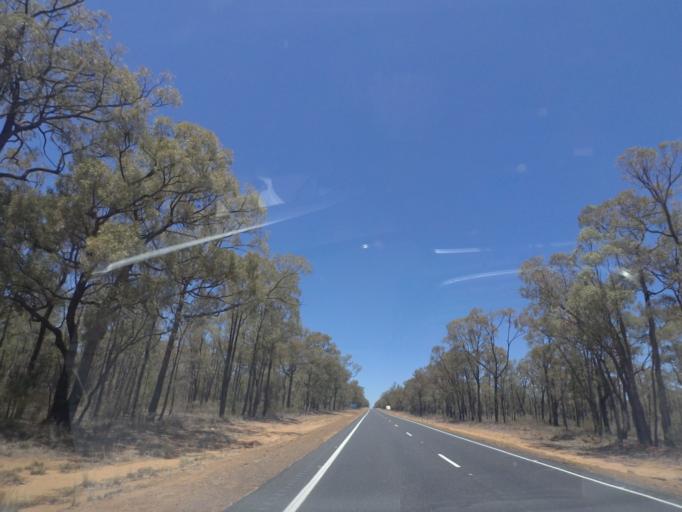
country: AU
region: New South Wales
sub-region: Narrabri
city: Narrabri
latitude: -30.7252
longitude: 149.5234
